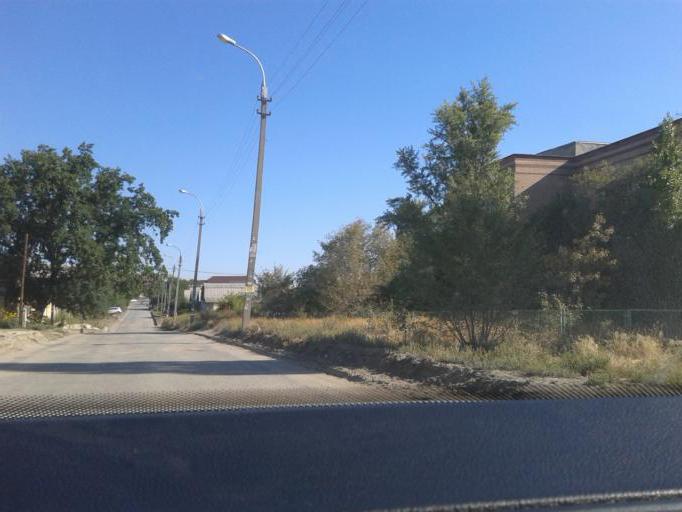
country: RU
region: Volgograd
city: Volgograd
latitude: 48.6132
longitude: 44.4139
